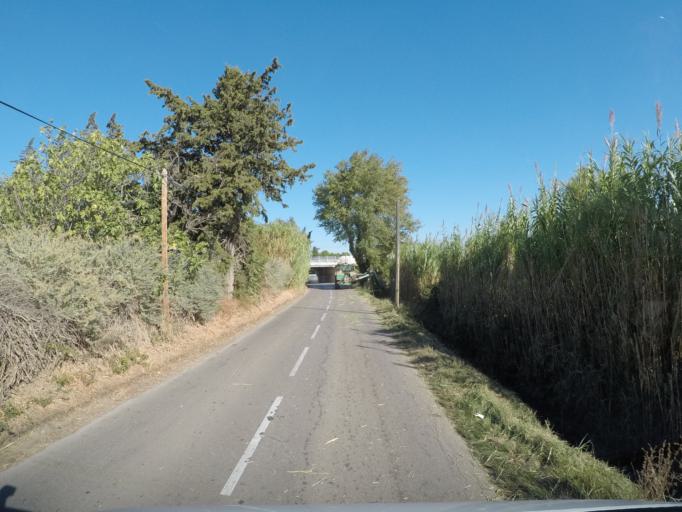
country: FR
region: Languedoc-Roussillon
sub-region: Departement de l'Aude
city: Narbonne
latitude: 43.1678
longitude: 3.0098
